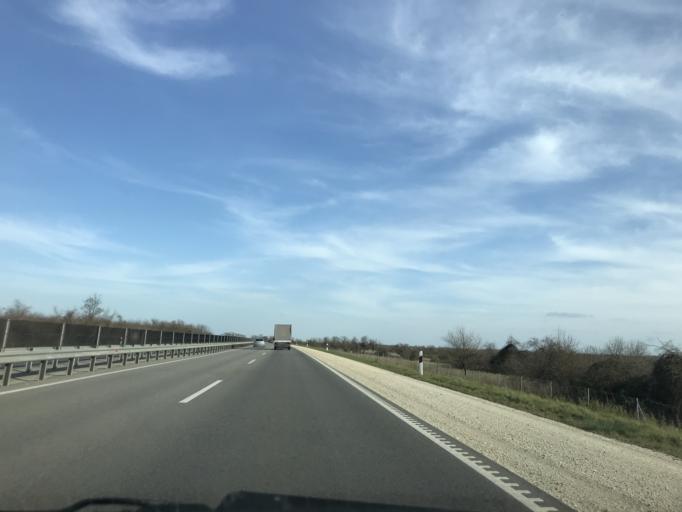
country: HU
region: Pest
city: Gomba
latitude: 47.3400
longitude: 19.5024
